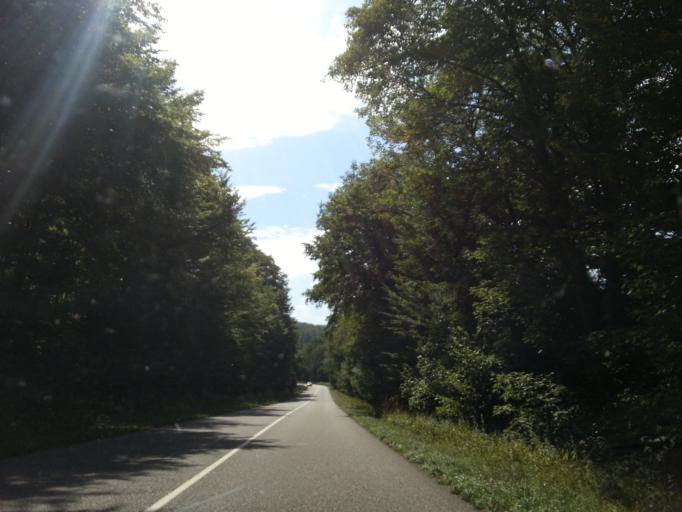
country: FR
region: Alsace
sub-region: Departement du Bas-Rhin
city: Lembach
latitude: 48.9896
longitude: 7.7788
